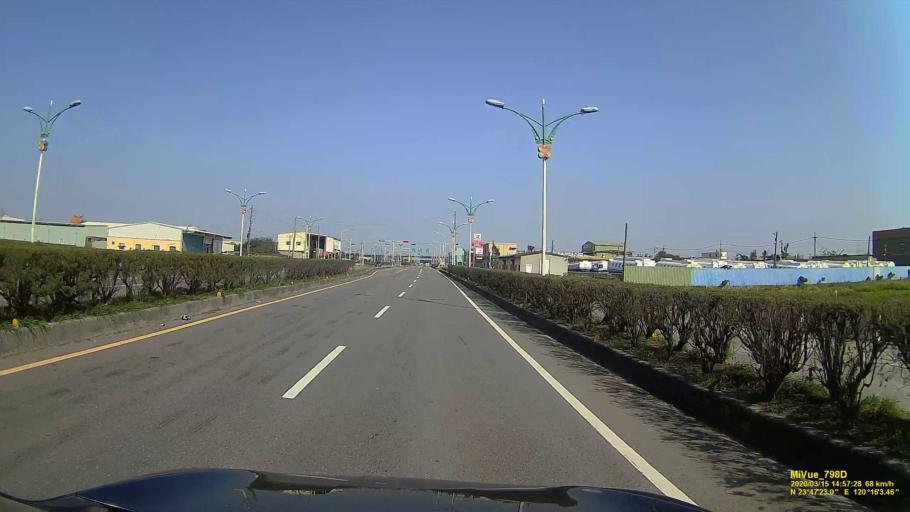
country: TW
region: Taiwan
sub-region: Yunlin
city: Douliu
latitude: 23.7897
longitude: 120.2680
